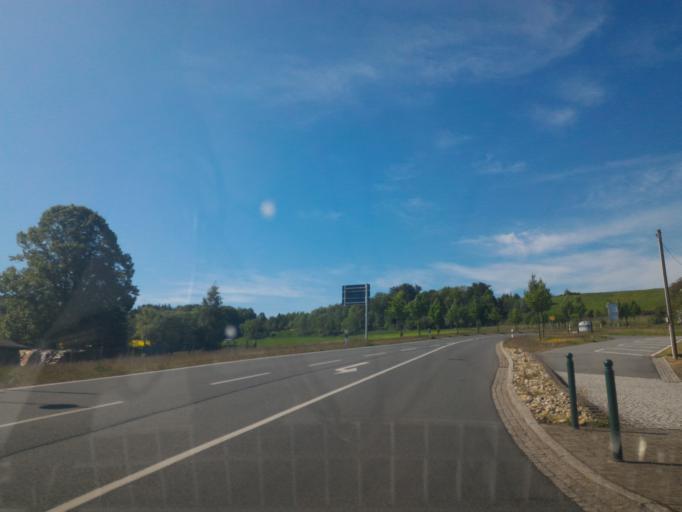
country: DE
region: Saxony
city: Leutersdorf
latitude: 50.9345
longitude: 14.6684
